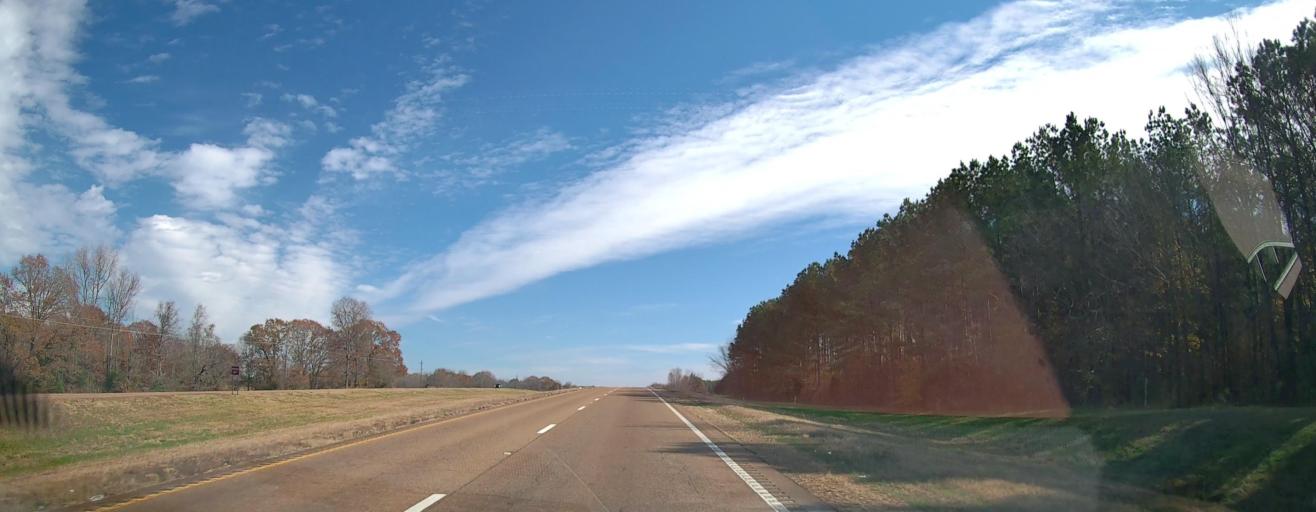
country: US
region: Mississippi
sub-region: Marshall County
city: Holly Springs
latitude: 34.9461
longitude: -89.3700
